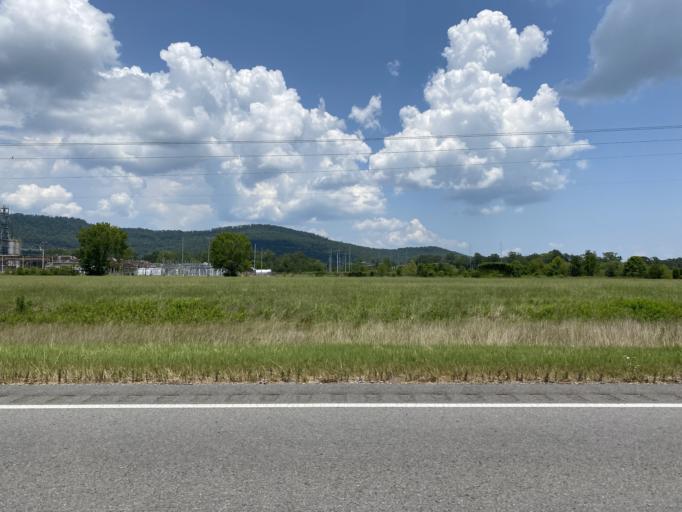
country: US
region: Alabama
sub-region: Jackson County
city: Scottsboro
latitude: 34.6157
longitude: -86.0838
